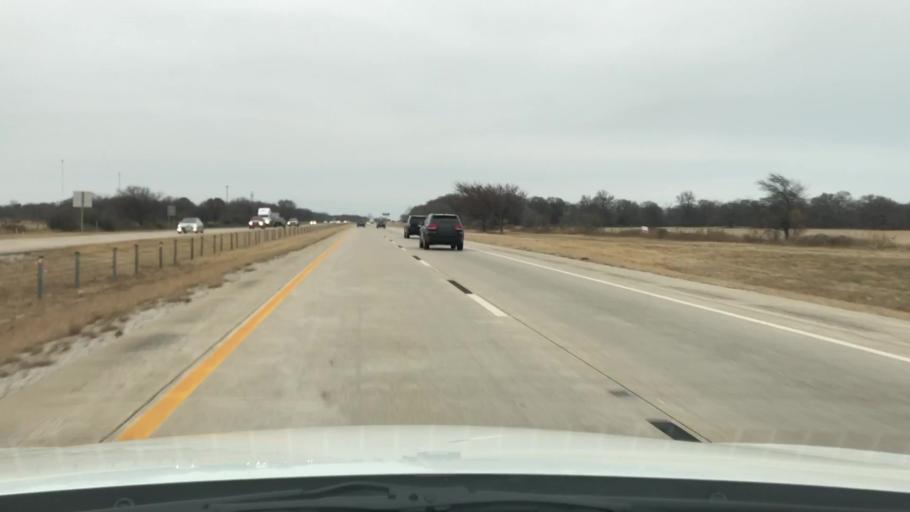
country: US
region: Oklahoma
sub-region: Love County
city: Marietta
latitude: 33.7974
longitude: -97.1349
